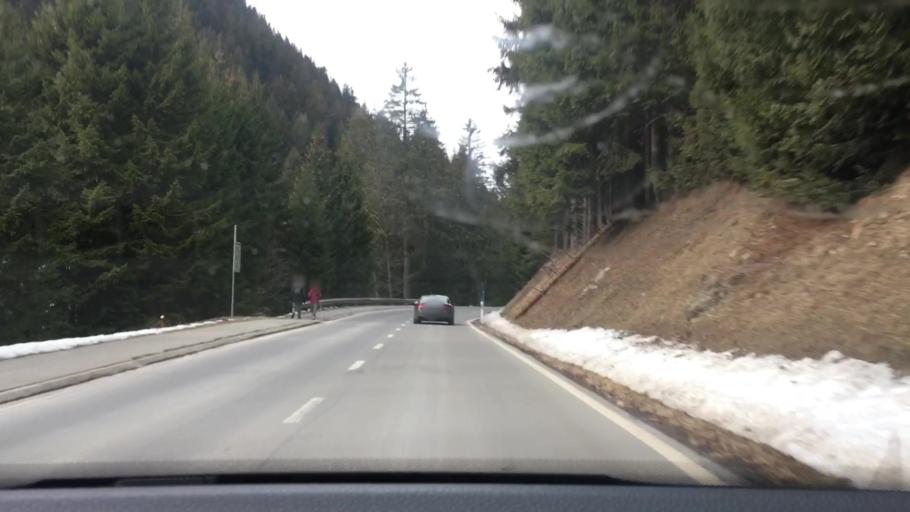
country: FR
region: Rhone-Alpes
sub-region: Departement de la Haute-Savoie
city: Chatel
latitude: 46.2473
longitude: 6.8488
